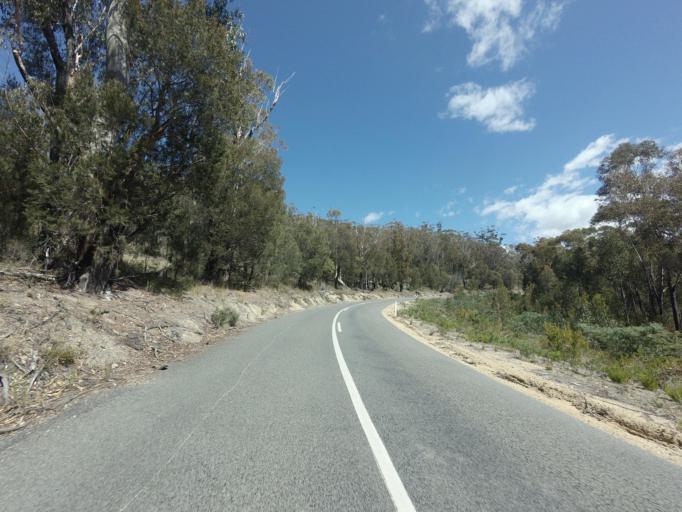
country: AU
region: Tasmania
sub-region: Break O'Day
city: St Helens
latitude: -41.6638
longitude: 148.2685
